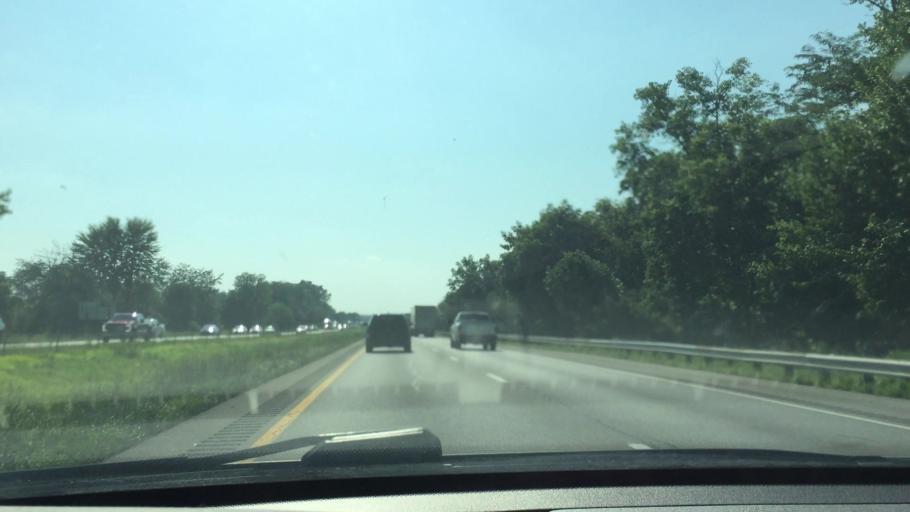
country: US
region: Ohio
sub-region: Fairfield County
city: Millersport
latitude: 39.9431
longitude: -82.5502
